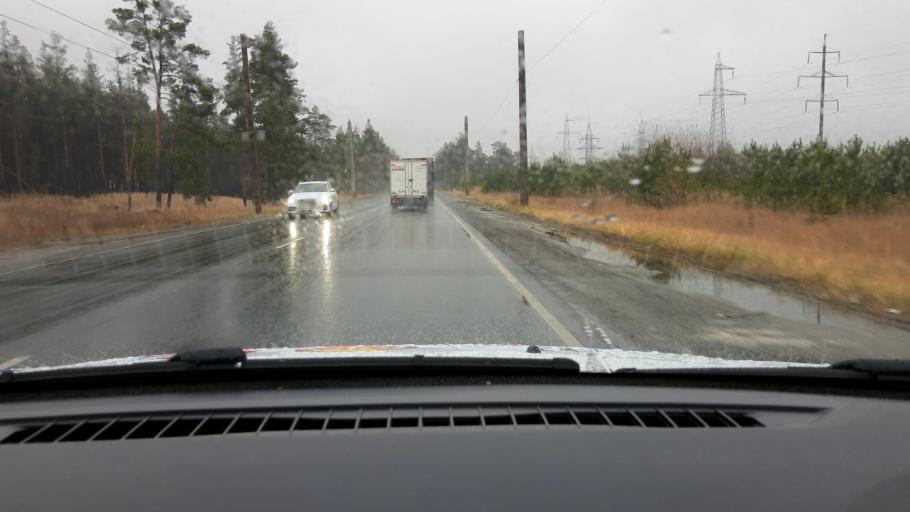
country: RU
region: Nizjnij Novgorod
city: Babino
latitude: 56.2738
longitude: 43.5522
